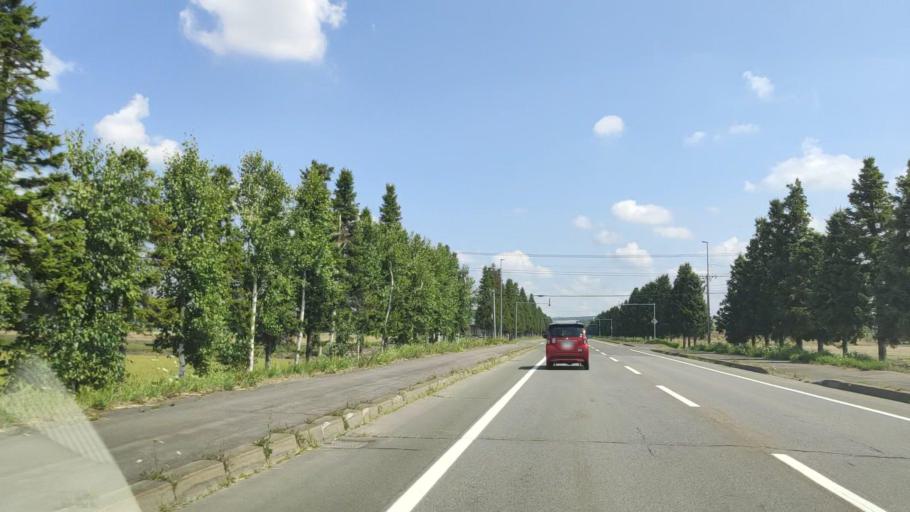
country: JP
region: Hokkaido
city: Shimo-furano
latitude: 43.4794
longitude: 142.4593
